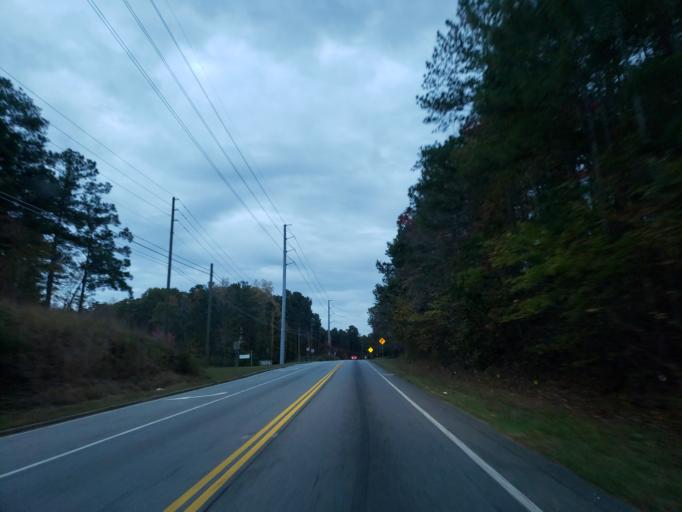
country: US
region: Georgia
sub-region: Paulding County
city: Hiram
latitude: 33.9525
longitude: -84.7378
